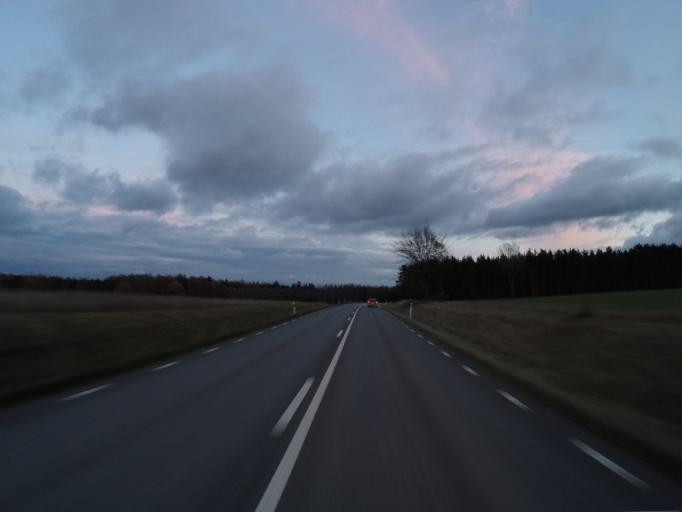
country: SE
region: Skane
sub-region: Kristianstads Kommun
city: Degeberga
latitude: 55.8183
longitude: 14.1263
